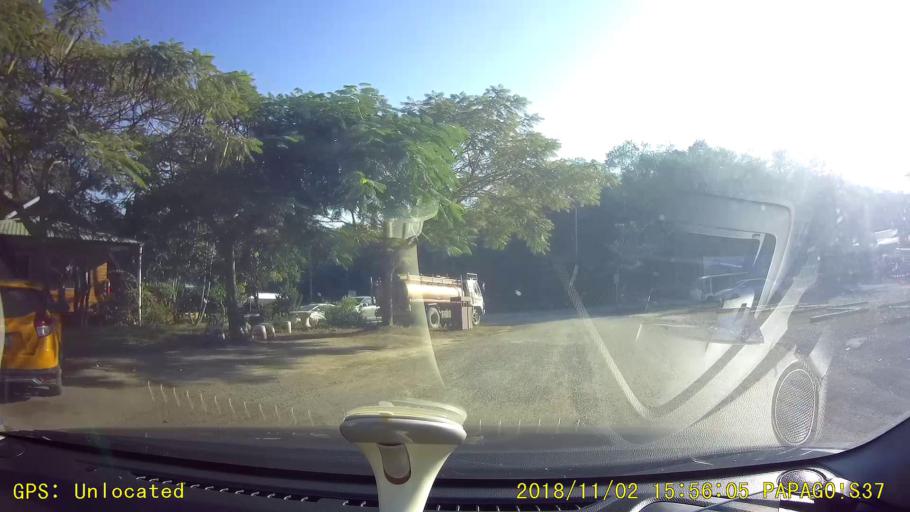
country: TH
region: Nakhon Ratchasima
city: Pak Chong
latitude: 14.7279
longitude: 101.3922
